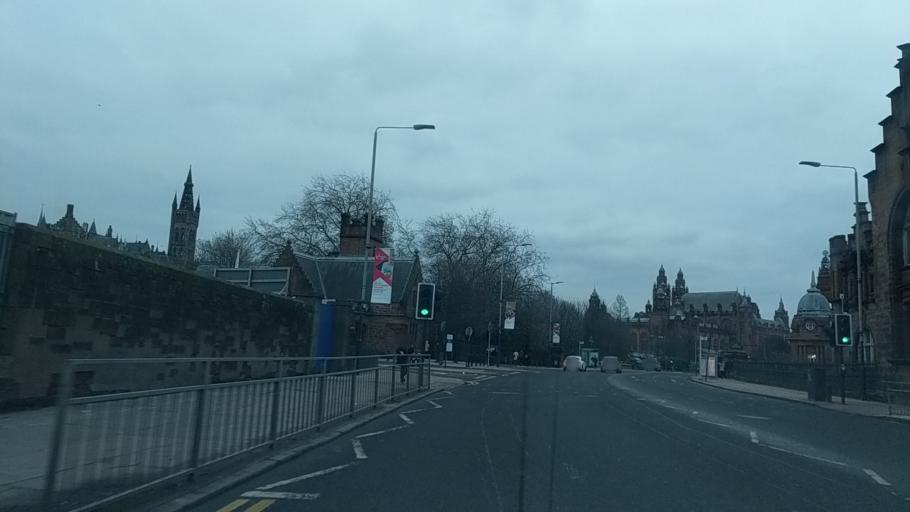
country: GB
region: Scotland
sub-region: Glasgow City
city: Glasgow
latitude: 55.8701
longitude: -4.2961
